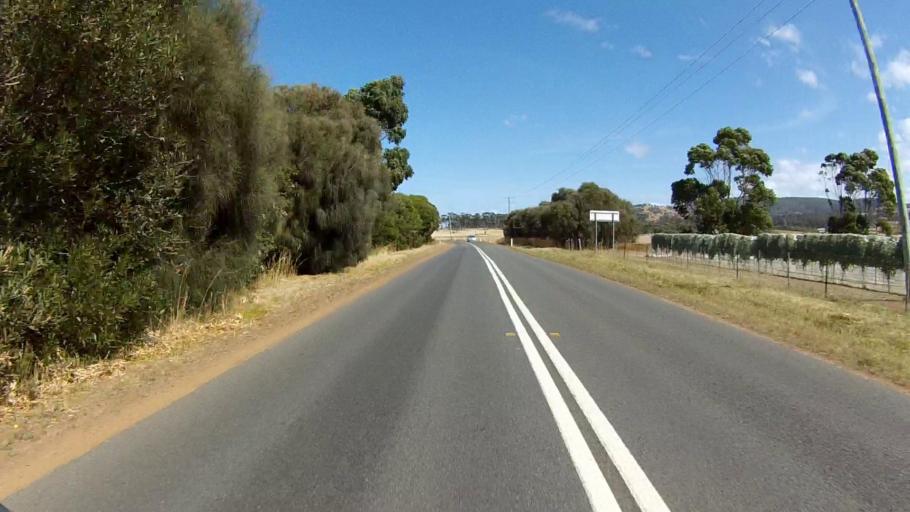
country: AU
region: Tasmania
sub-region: Sorell
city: Sorell
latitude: -42.2018
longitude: 148.0441
